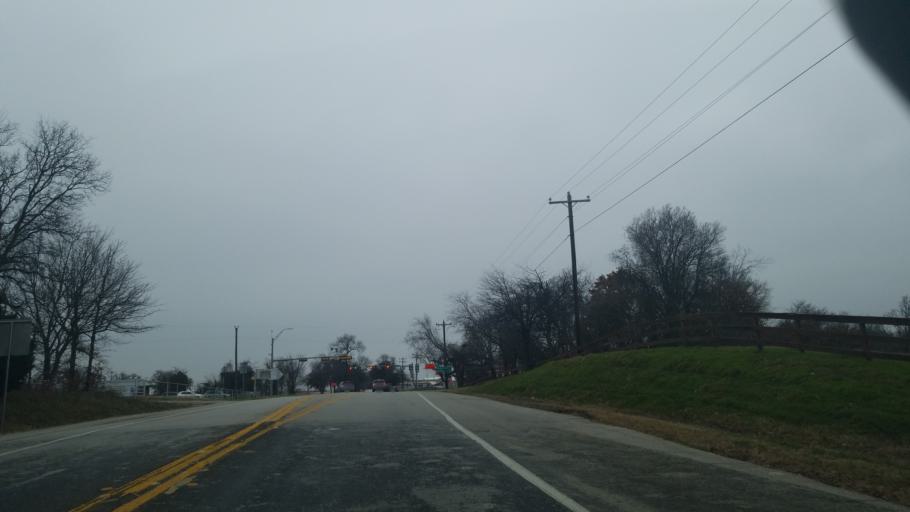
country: US
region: Texas
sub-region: Denton County
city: Bartonville
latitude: 33.1058
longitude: -97.1399
